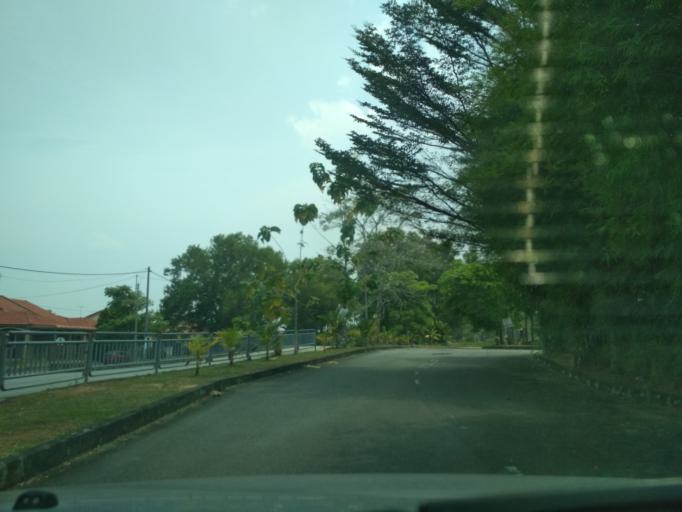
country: MY
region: Kedah
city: Kulim
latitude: 5.3585
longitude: 100.5367
